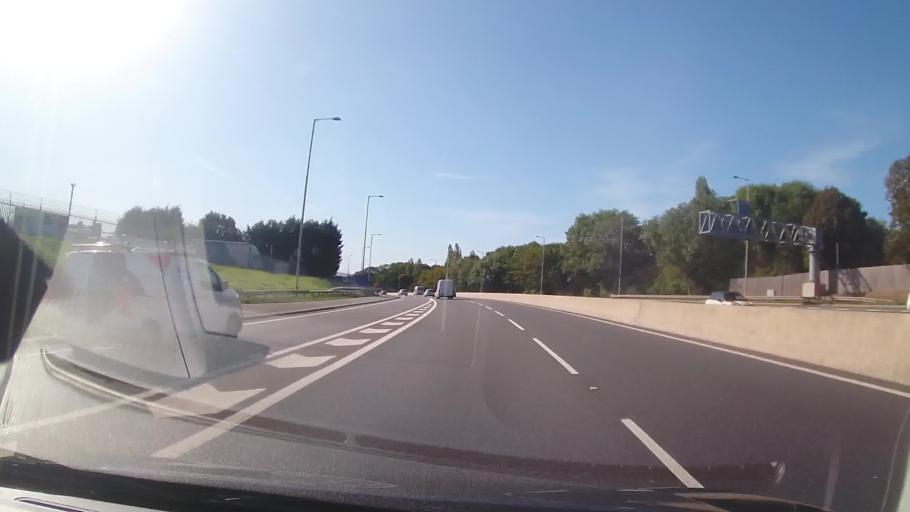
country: GB
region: England
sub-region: Warwickshire
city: Ryton on Dunsmore
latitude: 52.3790
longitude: -1.4717
